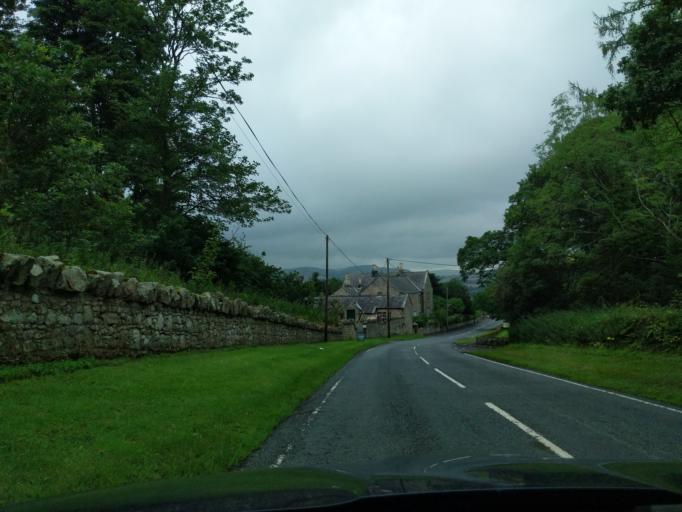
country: GB
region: England
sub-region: Northumberland
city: Ford
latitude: 55.6316
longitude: -2.0827
